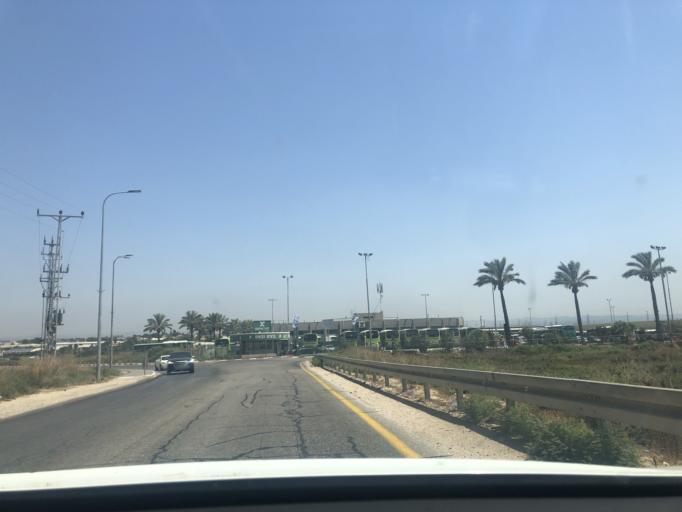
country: IL
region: Central District
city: Lod
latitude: 31.9321
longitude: 34.8938
